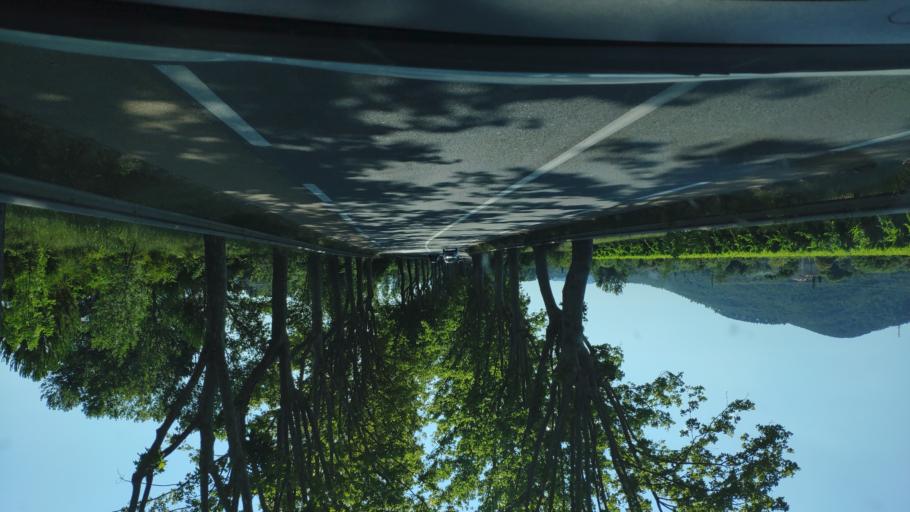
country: FR
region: Provence-Alpes-Cote d'Azur
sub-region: Departement du Var
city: Les Arcs
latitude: 43.4434
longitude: 6.4643
